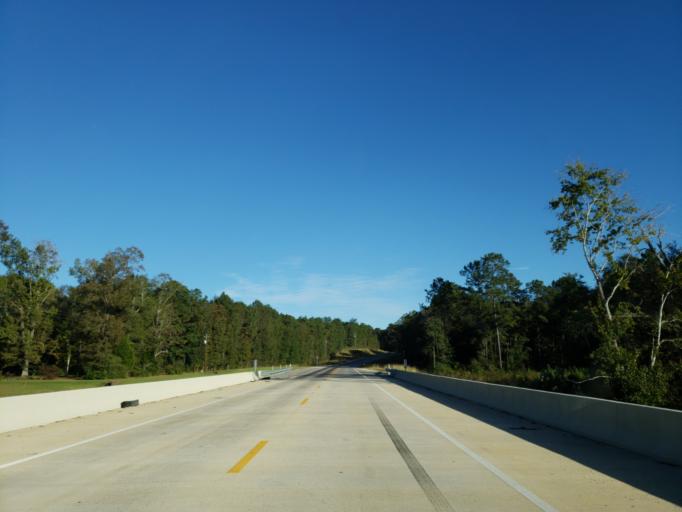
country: US
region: Mississippi
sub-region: Perry County
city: Richton
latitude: 31.3642
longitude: -88.8079
